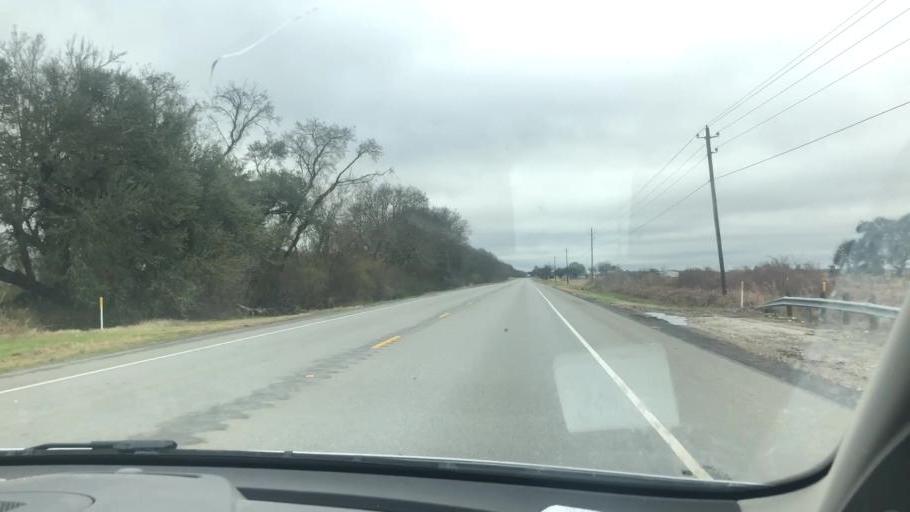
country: US
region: Texas
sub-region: Matagorda County
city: Bay City
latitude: 29.0749
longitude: -95.9724
